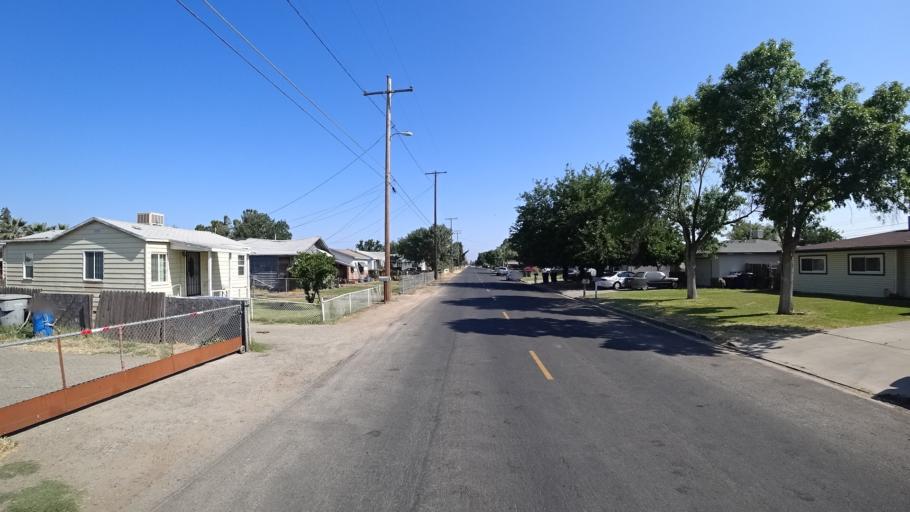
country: US
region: California
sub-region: Kings County
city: Home Garden
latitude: 36.3067
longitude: -119.6527
